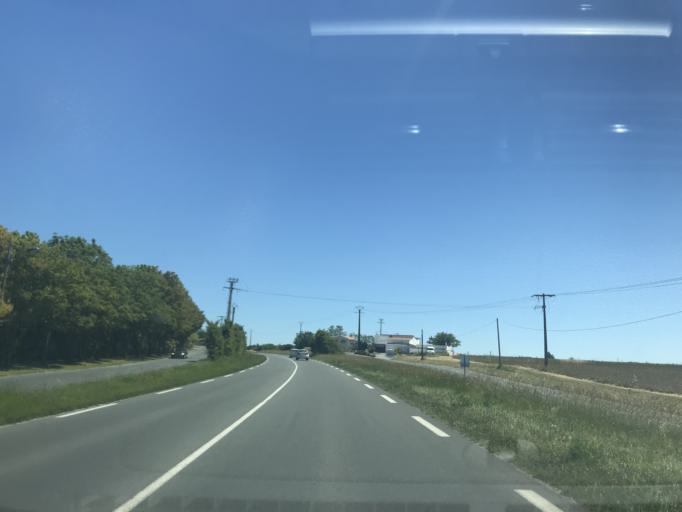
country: FR
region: Poitou-Charentes
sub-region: Departement de la Charente-Maritime
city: Vaux-sur-Mer
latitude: 45.6453
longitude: -1.0438
